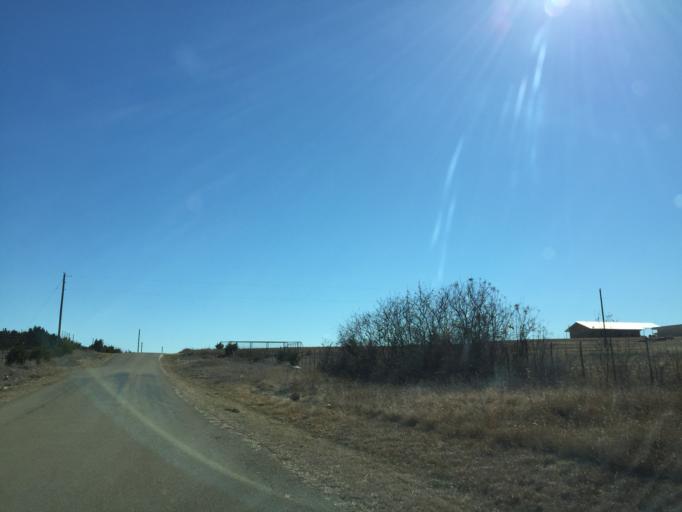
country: US
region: Texas
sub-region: Burnet County
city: Bertram
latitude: 30.8922
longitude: -98.1206
